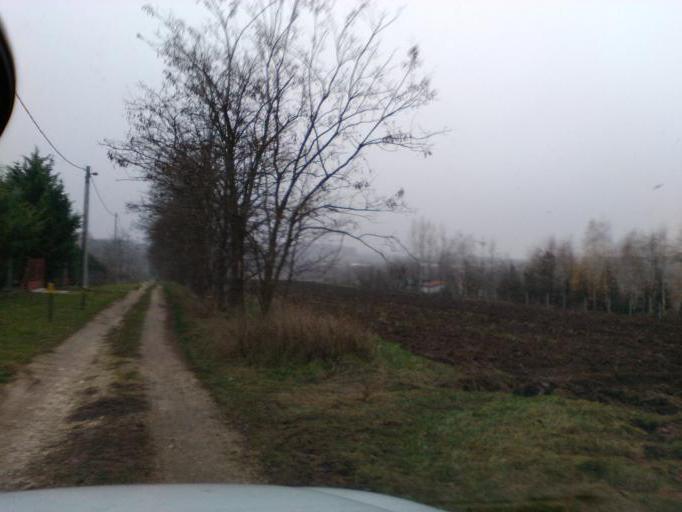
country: HU
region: Pest
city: Soskut
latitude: 47.4031
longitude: 18.7903
